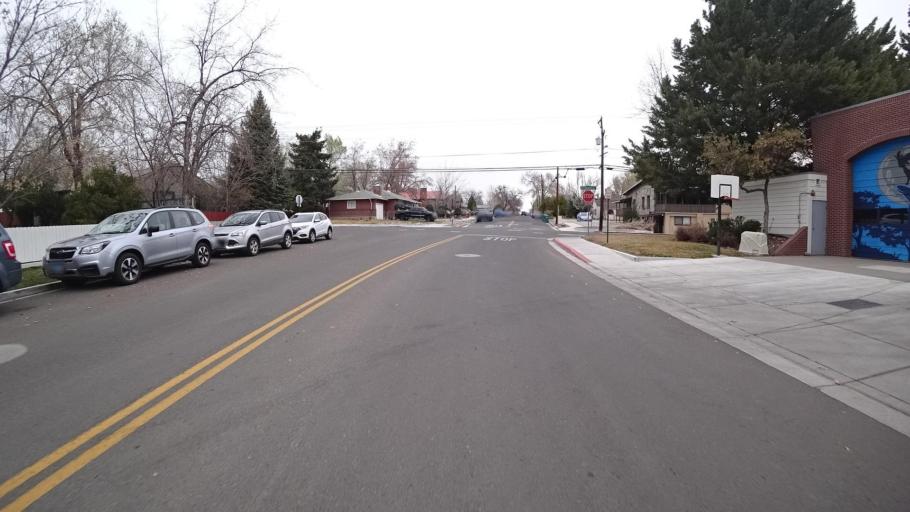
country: US
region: Nevada
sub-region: Washoe County
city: Reno
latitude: 39.5379
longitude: -119.8237
